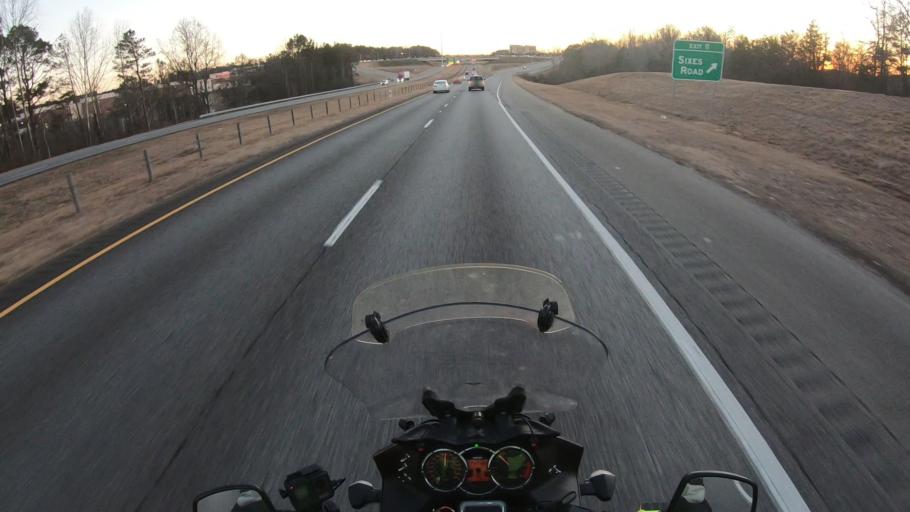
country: US
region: Georgia
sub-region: Cherokee County
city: Holly Springs
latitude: 34.1509
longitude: -84.5148
